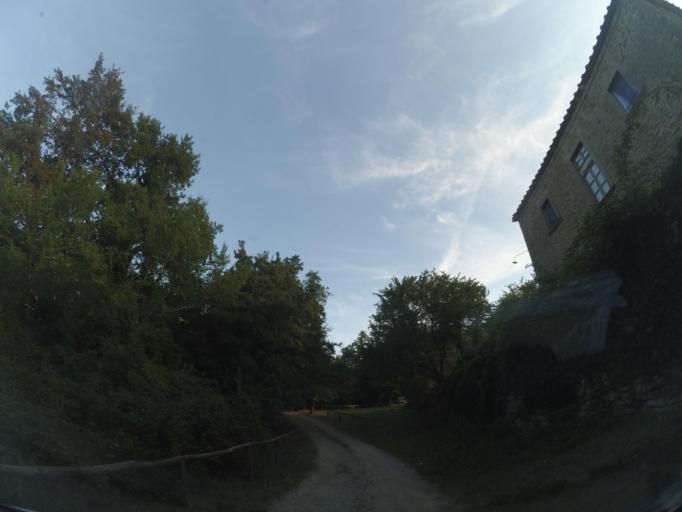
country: IT
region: Tuscany
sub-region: Province of Arezzo
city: Castiglion Fibocchi
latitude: 43.5583
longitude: 11.7828
